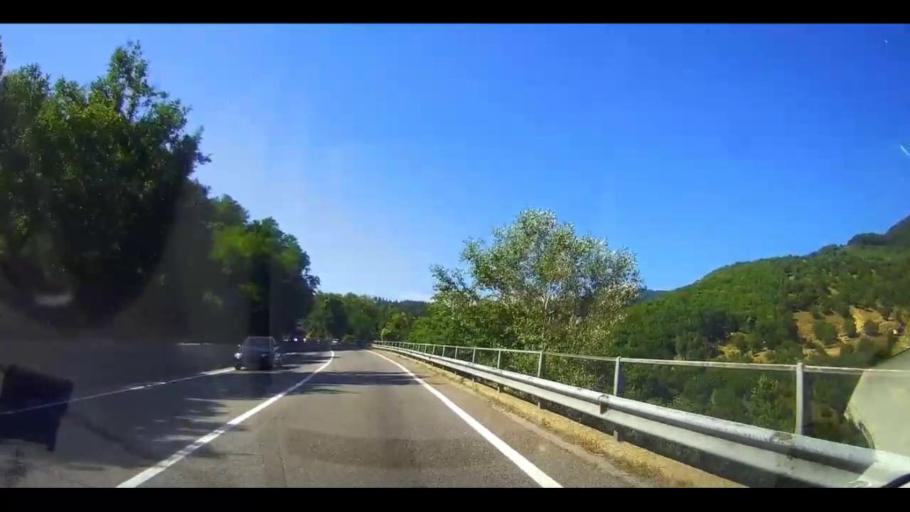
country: IT
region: Calabria
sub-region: Provincia di Cosenza
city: Spezzano Piccolo
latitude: 39.2967
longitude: 16.3549
